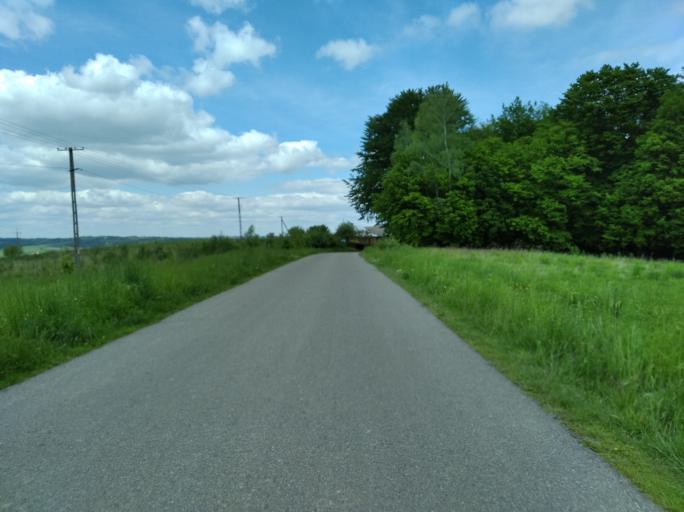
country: PL
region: Subcarpathian Voivodeship
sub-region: Powiat ropczycko-sedziszowski
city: Wielopole Skrzynskie
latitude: 49.9305
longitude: 21.6012
